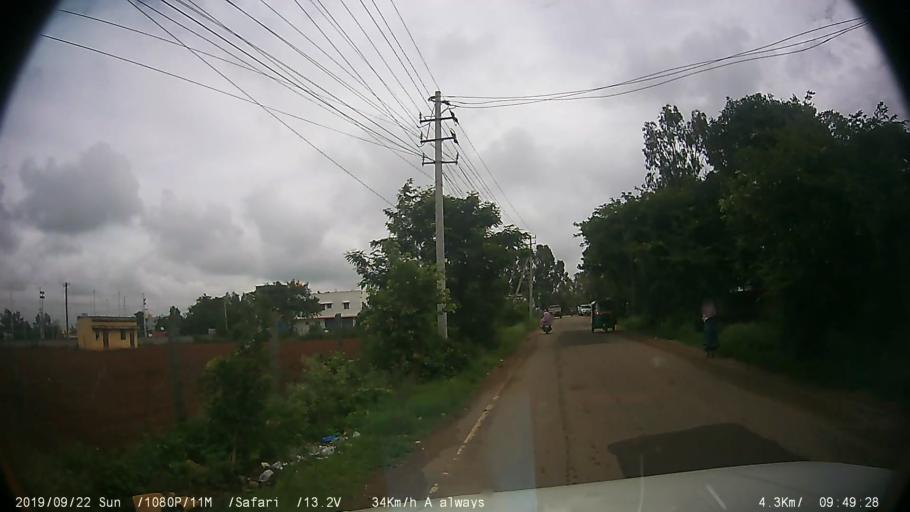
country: IN
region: Karnataka
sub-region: Bangalore Urban
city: Anekal
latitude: 12.8185
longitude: 77.6507
